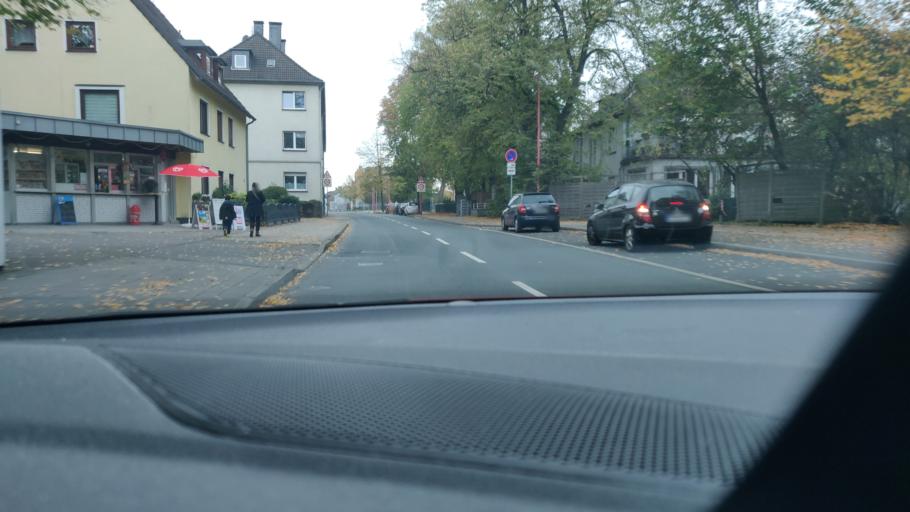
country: DE
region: North Rhine-Westphalia
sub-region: Regierungsbezirk Dusseldorf
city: Velbert
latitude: 51.3428
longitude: 7.0505
